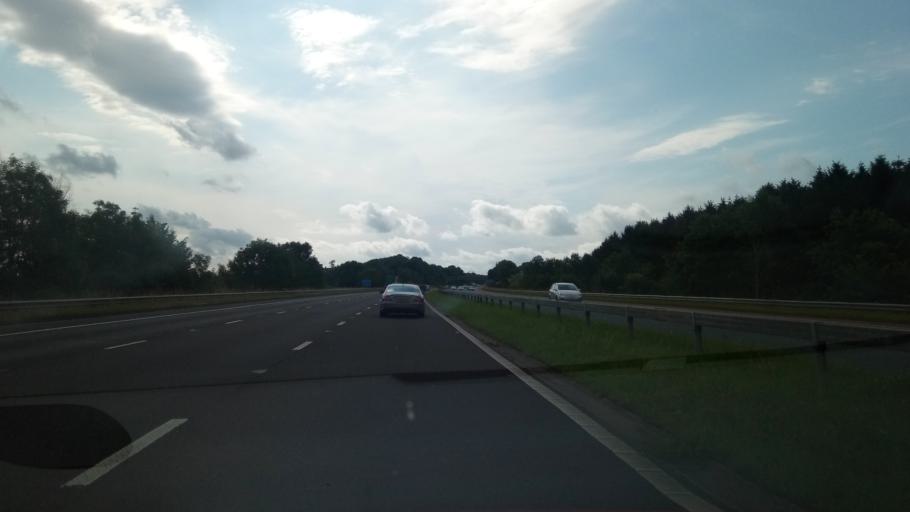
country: GB
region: England
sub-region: Cumbria
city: Penrith
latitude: 54.6412
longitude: -2.7346
